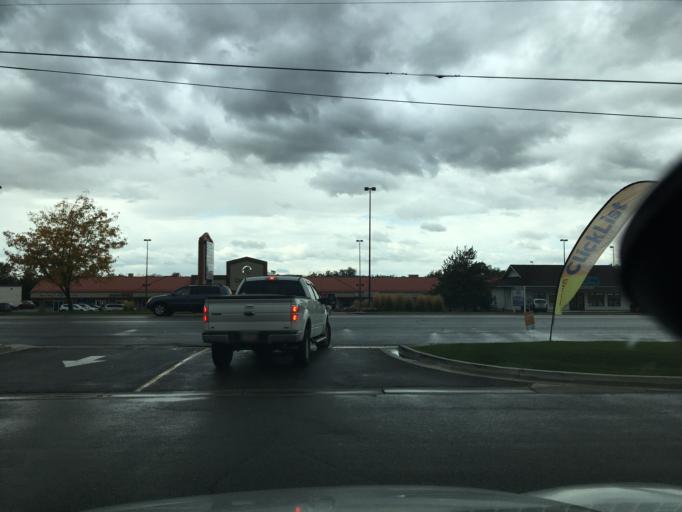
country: US
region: Utah
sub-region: Davis County
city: Layton
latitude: 41.0611
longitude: -111.9446
